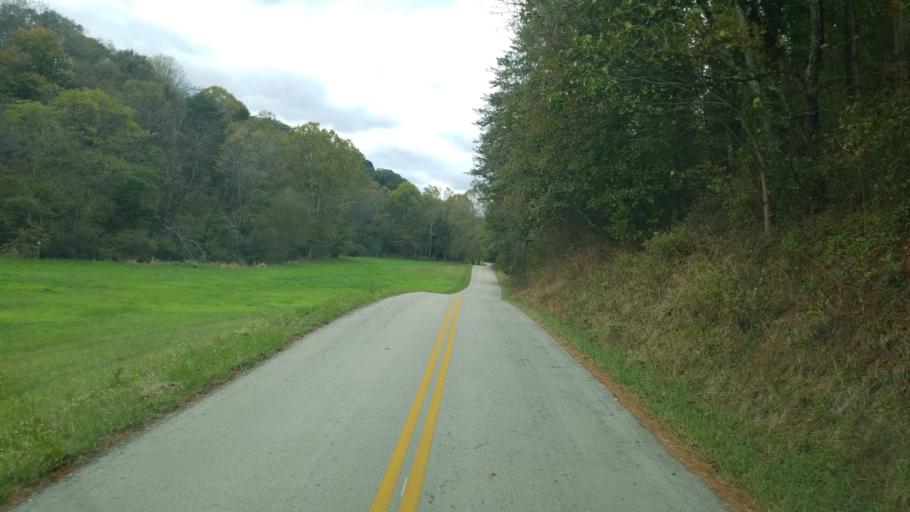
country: US
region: Ohio
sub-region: Jackson County
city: Wellston
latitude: 39.1650
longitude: -82.6324
